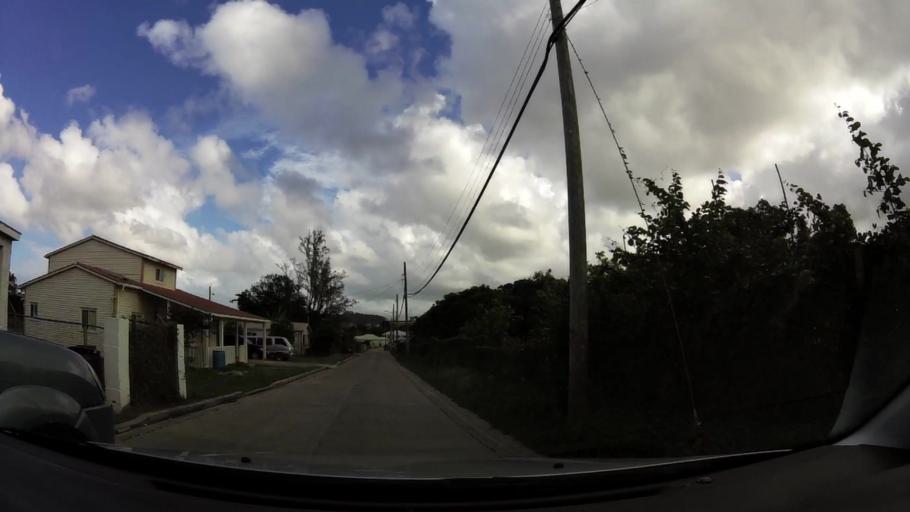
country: AG
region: Saint John
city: Saint John's
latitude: 17.1031
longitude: -61.8408
